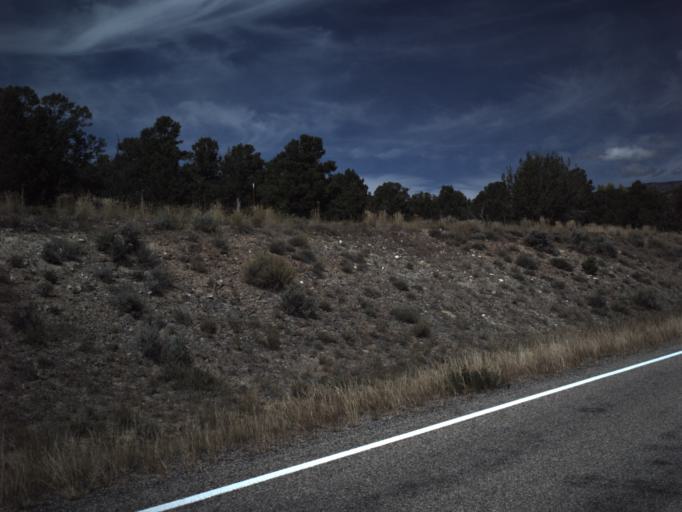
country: US
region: Utah
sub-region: Wayne County
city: Loa
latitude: 37.9611
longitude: -111.4346
